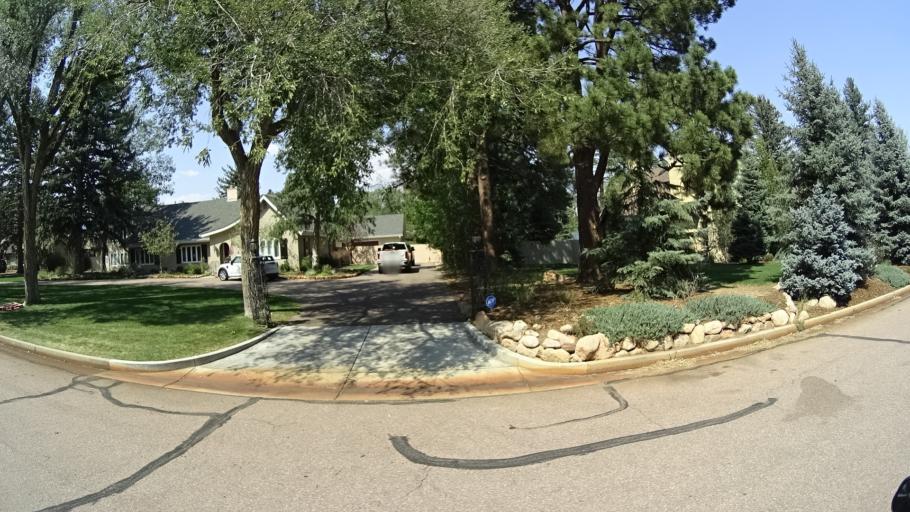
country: US
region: Colorado
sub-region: El Paso County
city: Colorado Springs
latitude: 38.7951
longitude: -104.8379
